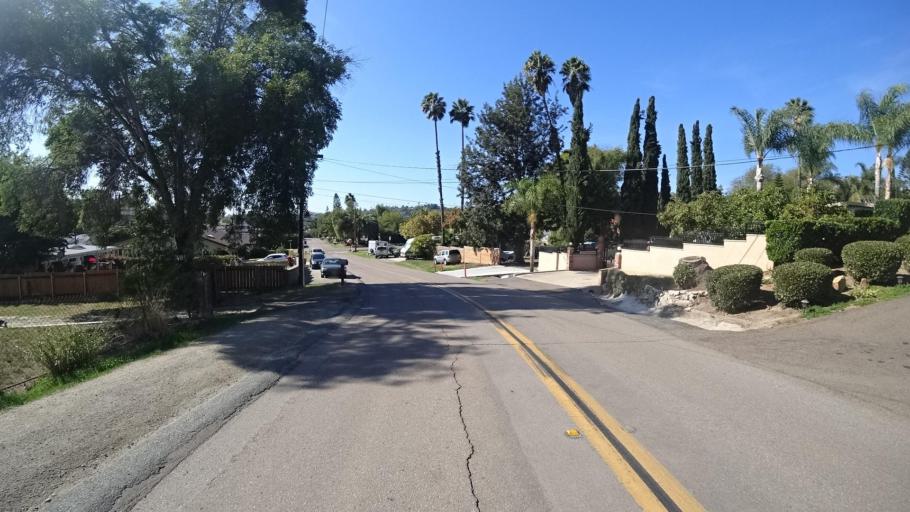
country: US
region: California
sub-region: San Diego County
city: Casa de Oro-Mount Helix
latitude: 32.7510
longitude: -116.9794
